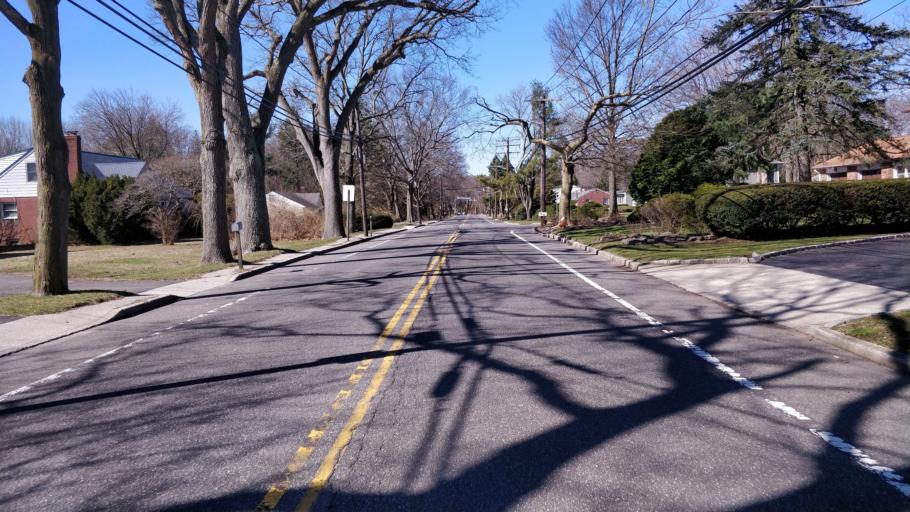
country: US
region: New York
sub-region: Suffolk County
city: Elwood
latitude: 40.8464
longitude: -73.3308
